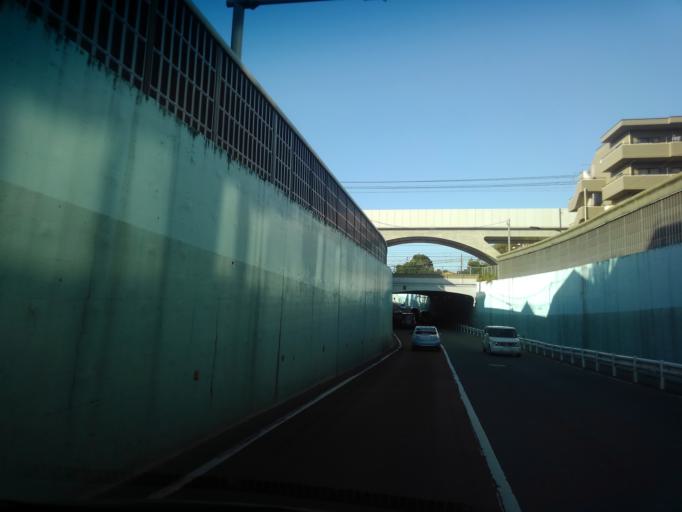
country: JP
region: Tokyo
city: Kokubunji
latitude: 35.7001
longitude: 139.4978
